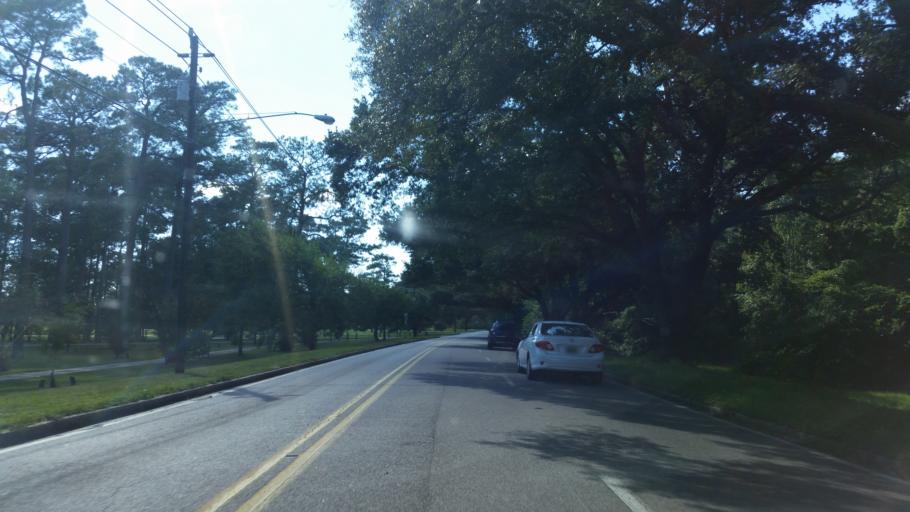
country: US
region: Alabama
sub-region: Mobile County
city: Prichard
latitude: 30.7090
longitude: -88.1566
